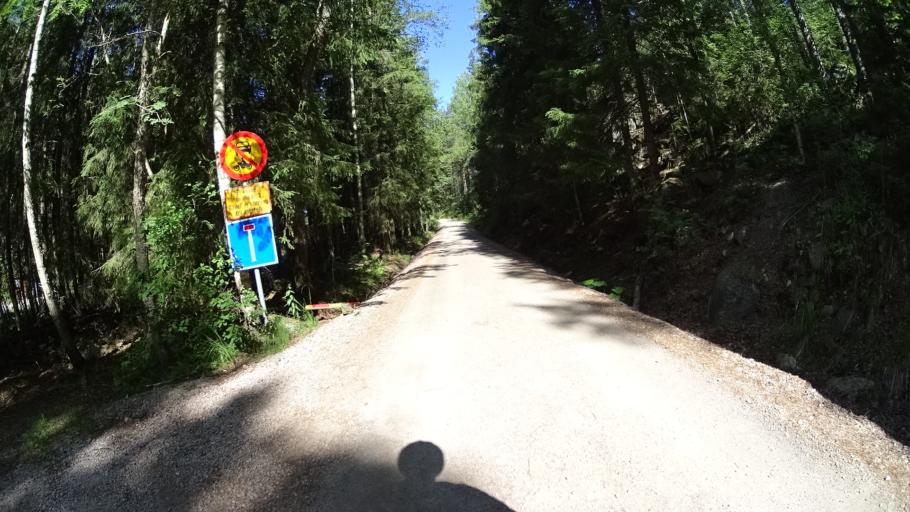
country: FI
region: Uusimaa
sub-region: Helsinki
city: Espoo
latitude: 60.3100
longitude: 24.5172
